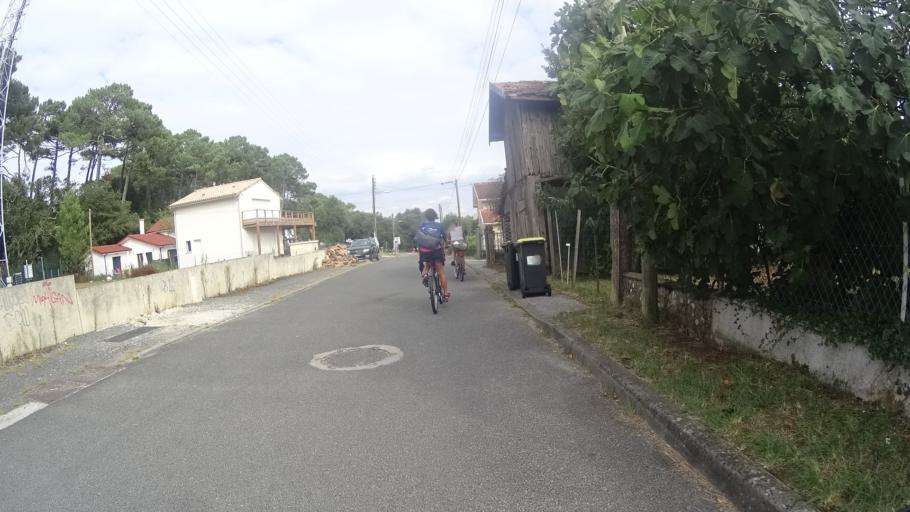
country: FR
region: Aquitaine
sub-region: Departement de la Gironde
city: Lacanau
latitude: 45.0032
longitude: -1.1362
